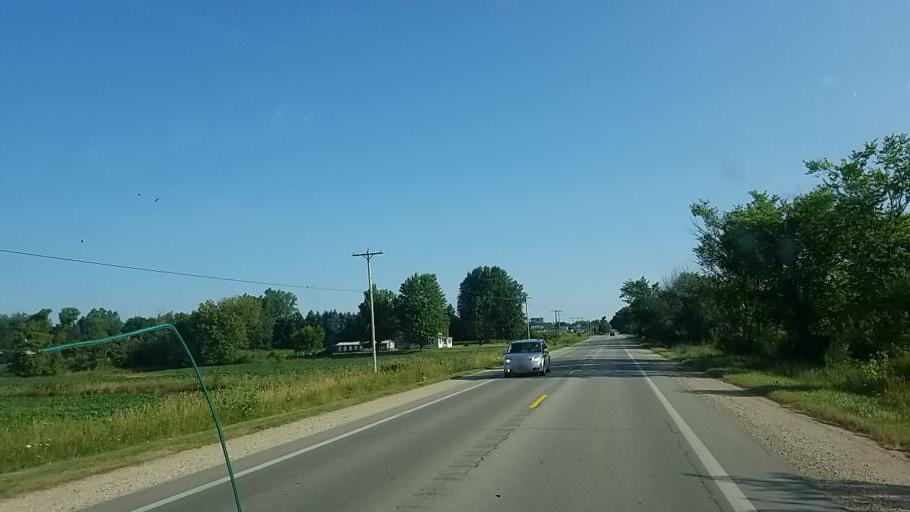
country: US
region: Michigan
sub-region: Newaygo County
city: Fremont
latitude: 43.4433
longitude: -85.9399
